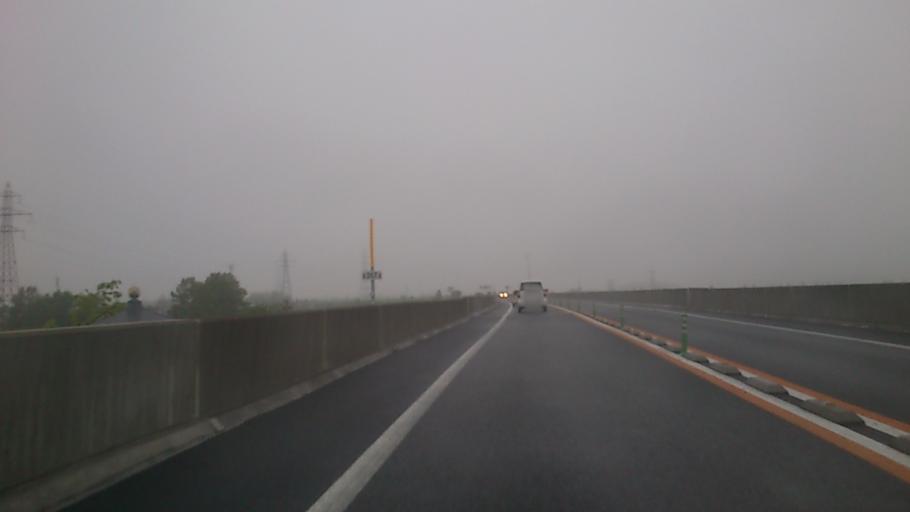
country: JP
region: Hokkaido
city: Kushiro
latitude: 43.0166
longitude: 144.4225
